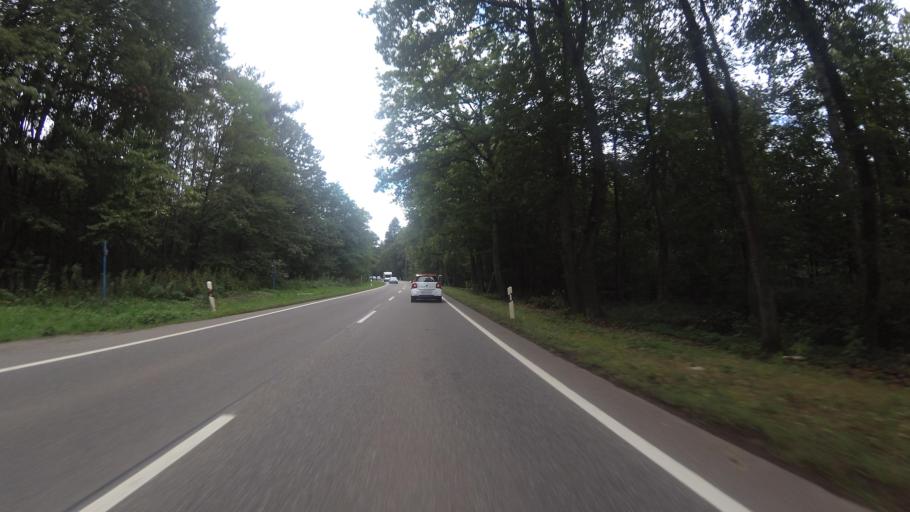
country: FR
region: Lorraine
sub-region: Departement de la Moselle
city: Petite-Rosselle
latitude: 49.2286
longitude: 6.8620
